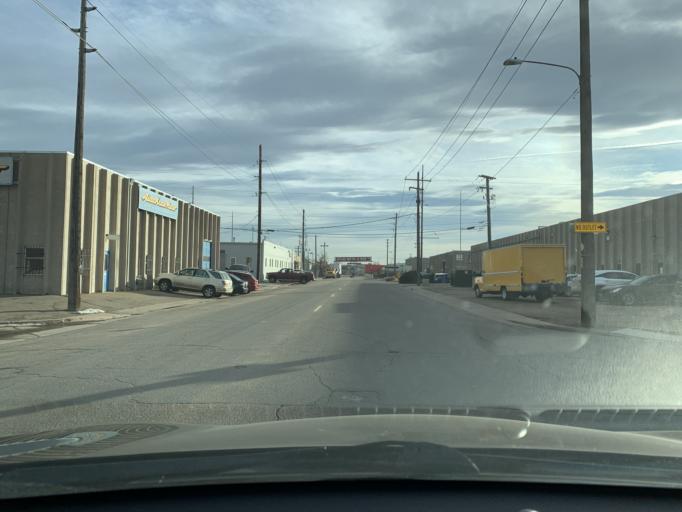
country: US
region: Colorado
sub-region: Denver County
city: Denver
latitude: 39.7362
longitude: -105.0123
